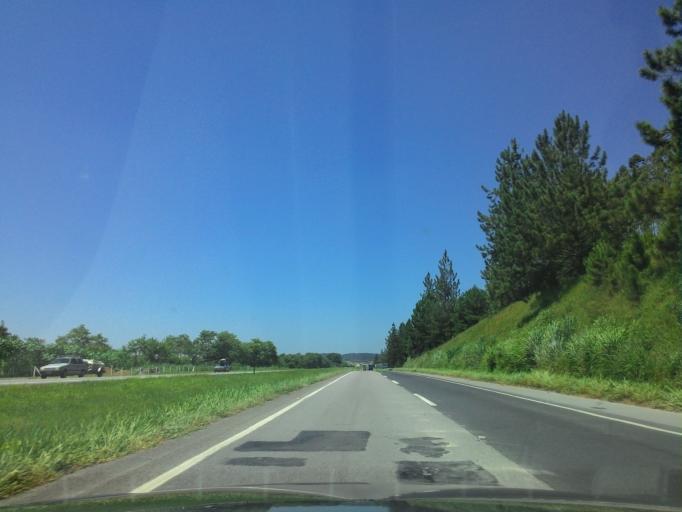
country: BR
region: Sao Paulo
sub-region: Jacupiranga
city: Jacupiranga
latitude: -24.7169
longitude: -48.0354
